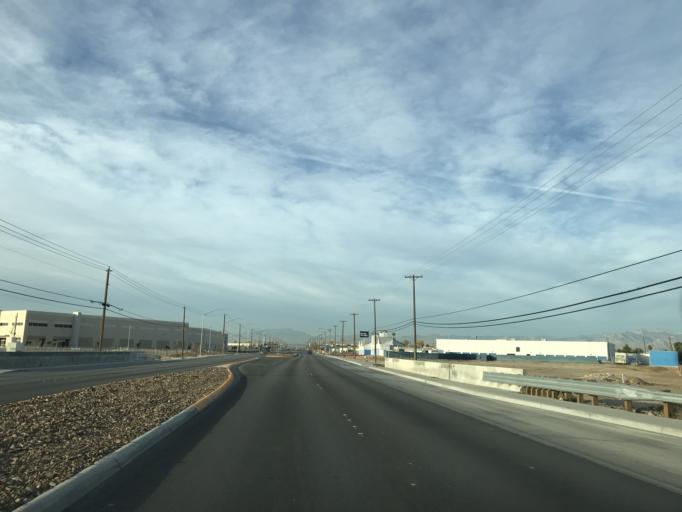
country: US
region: Nevada
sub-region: Clark County
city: Sunrise Manor
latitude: 36.2291
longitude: -115.0740
